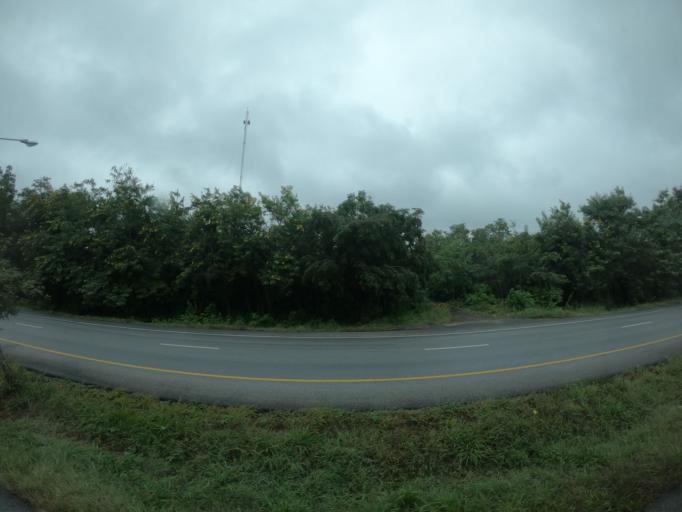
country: TH
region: Nakhon Ratchasima
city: Non Daeng
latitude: 15.3592
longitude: 102.4514
